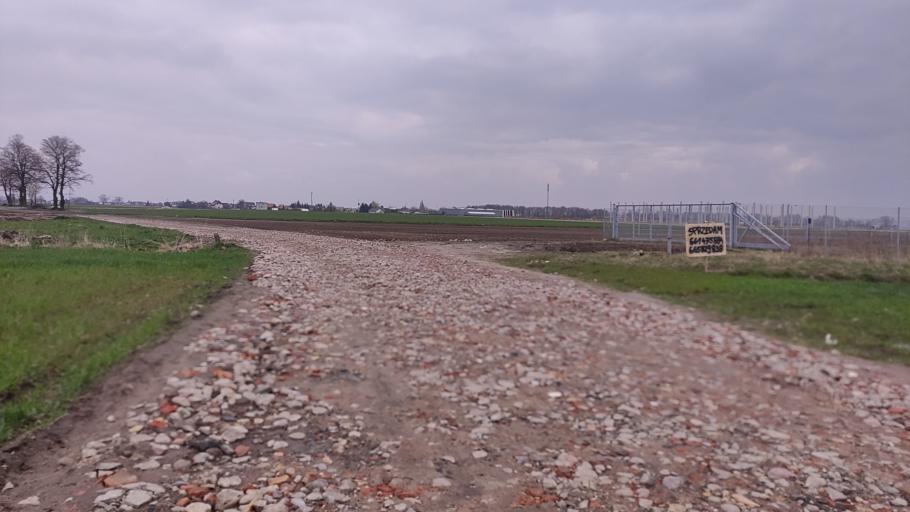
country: PL
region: Greater Poland Voivodeship
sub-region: Powiat poznanski
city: Swarzedz
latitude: 52.4041
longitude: 17.1435
